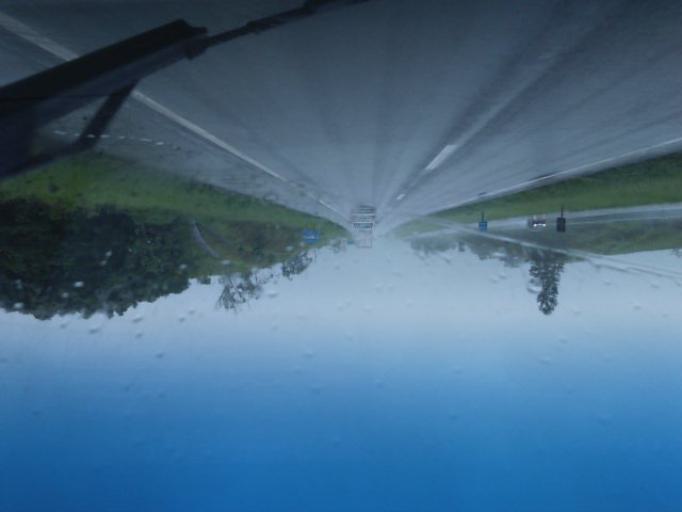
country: BR
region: Sao Paulo
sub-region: Pariquera-Acu
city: Pariquera Acu
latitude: -24.6377
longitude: -47.9114
